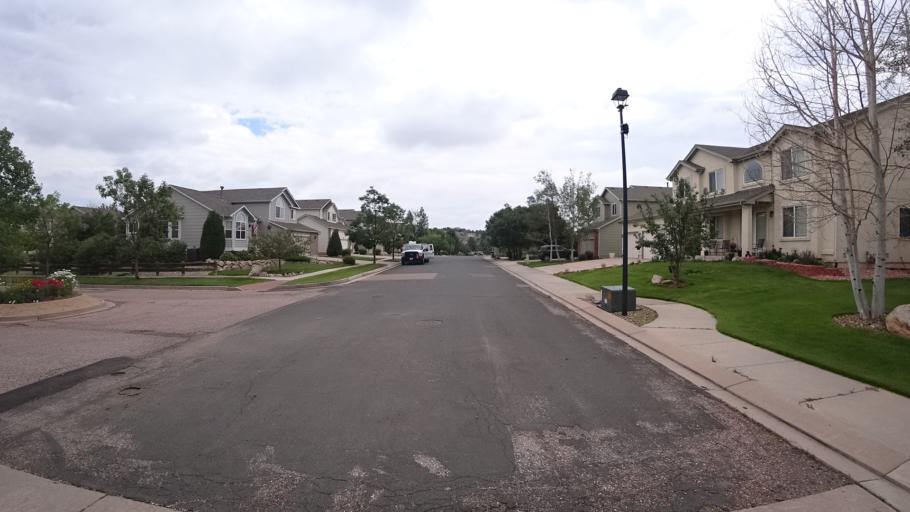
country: US
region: Colorado
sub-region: El Paso County
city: Gleneagle
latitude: 39.0065
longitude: -104.8018
